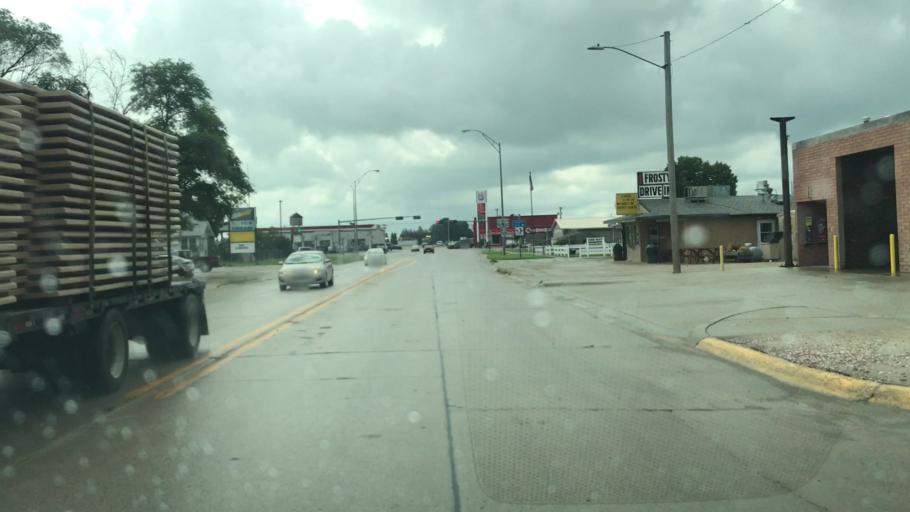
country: US
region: Nebraska
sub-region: Cherry County
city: Valentine
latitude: 42.8693
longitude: -100.5505
